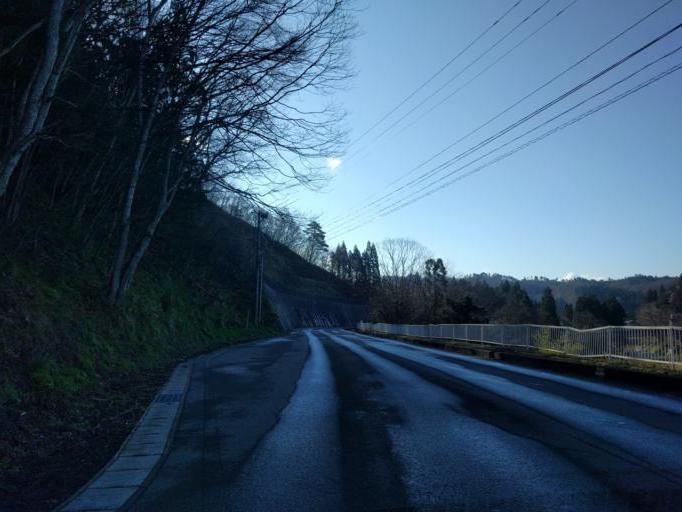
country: JP
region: Fukushima
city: Kitakata
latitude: 37.6805
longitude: 139.7906
